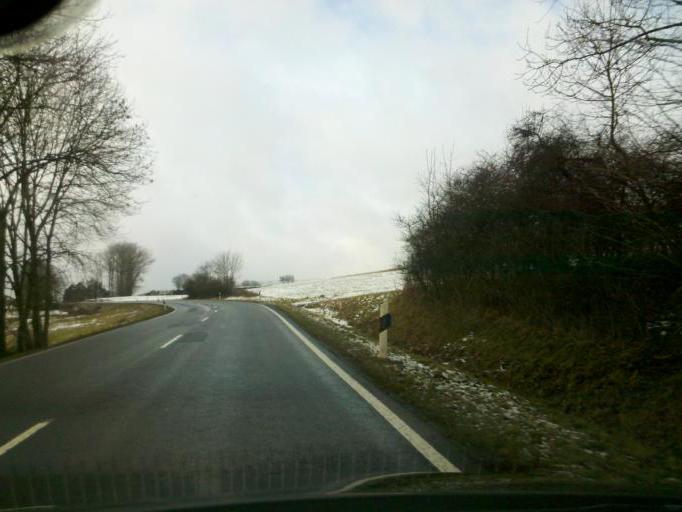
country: DE
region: Hesse
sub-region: Regierungsbezirk Giessen
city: Breidenbach
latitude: 50.8400
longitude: 8.4923
